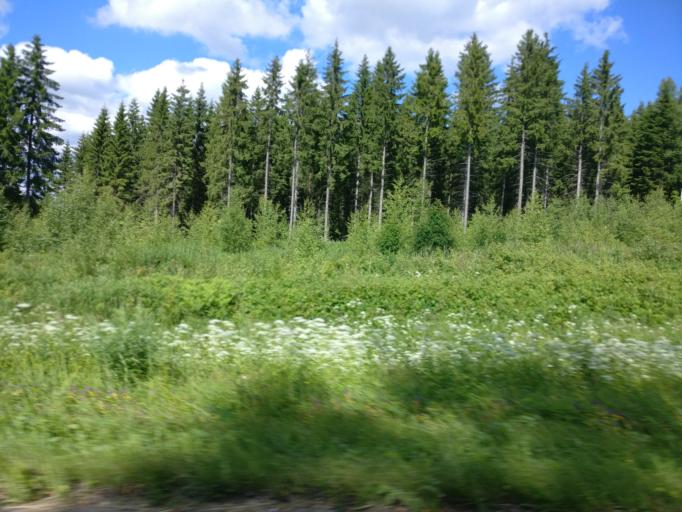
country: FI
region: Southern Savonia
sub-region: Savonlinna
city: Kerimaeki
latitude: 61.8556
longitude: 29.1636
